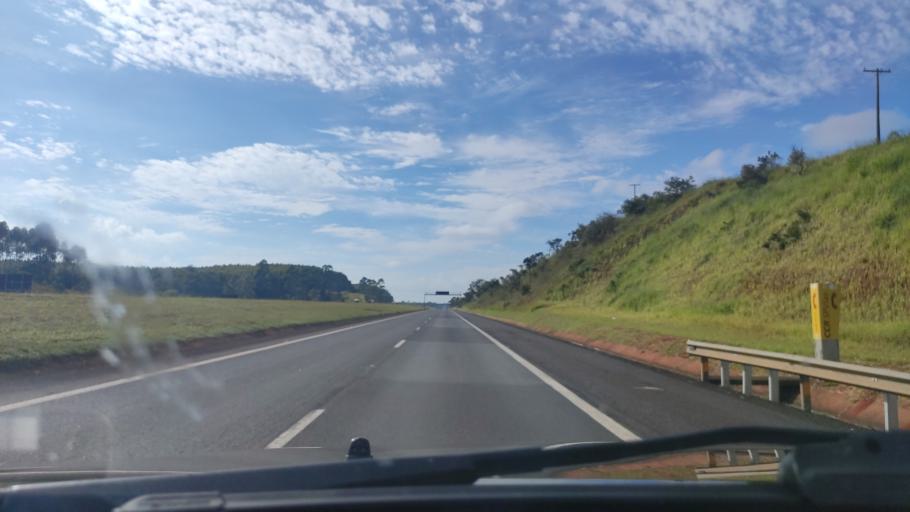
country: BR
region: Sao Paulo
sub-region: Itatinga
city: Itatinga
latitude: -23.0690
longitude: -48.5464
